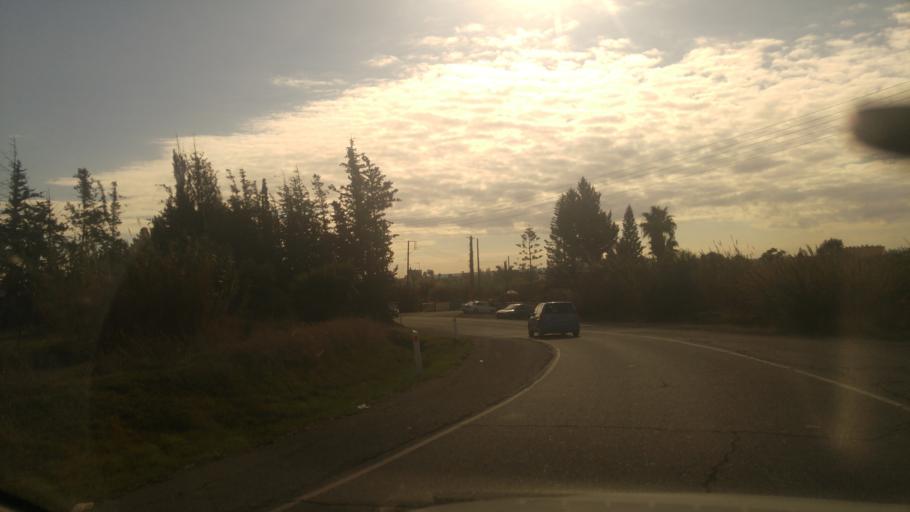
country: CY
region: Limassol
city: Erimi
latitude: 34.6735
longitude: 32.9243
